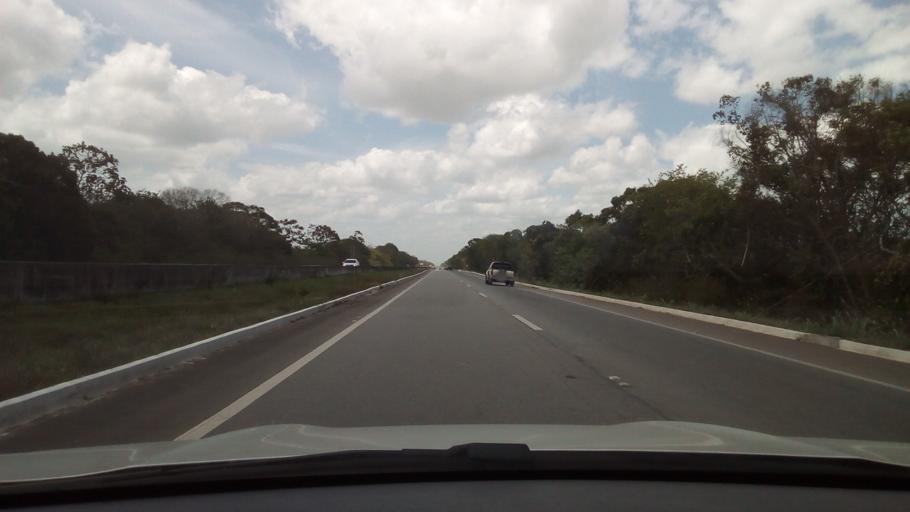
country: BR
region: Paraiba
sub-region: Mamanguape
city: Mamanguape
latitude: -6.9131
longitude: -35.1135
